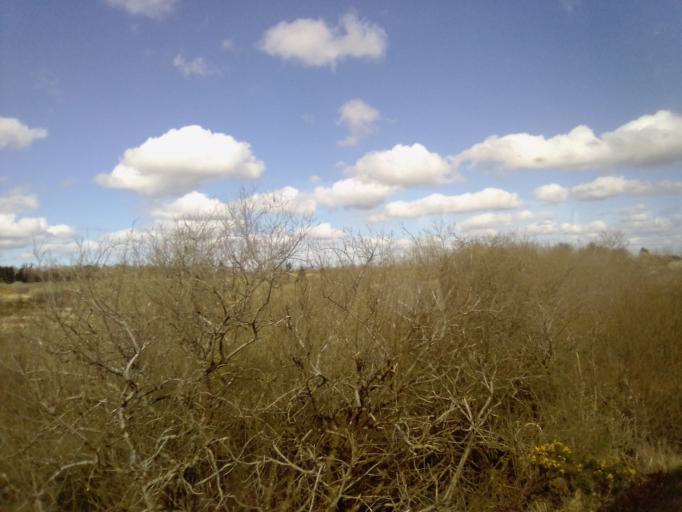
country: IE
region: Munster
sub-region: County Cork
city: Millstreet
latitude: 52.0857
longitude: -9.2229
